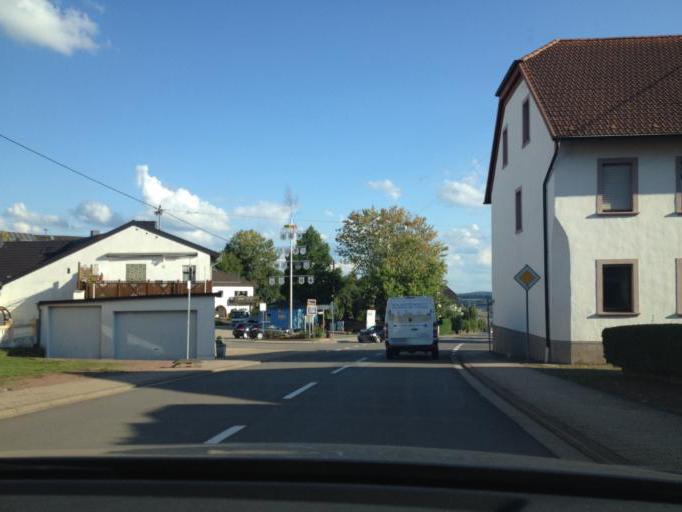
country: DE
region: Saarland
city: Eppelborn
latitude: 49.4742
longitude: 6.9617
